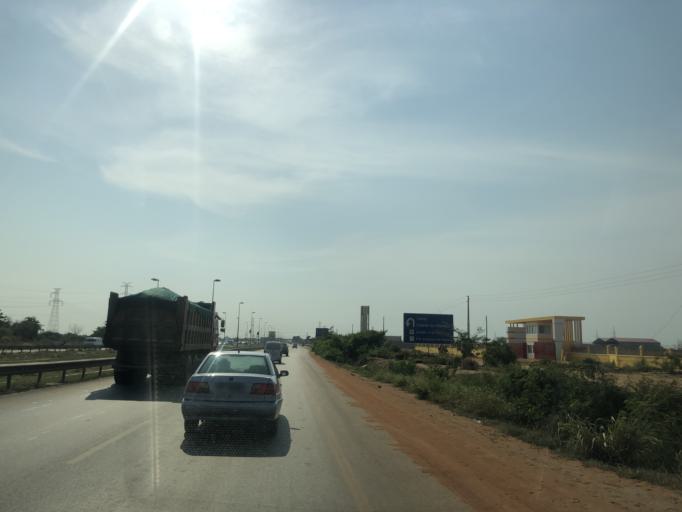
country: AO
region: Luanda
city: Luanda
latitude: -8.9732
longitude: 13.2673
